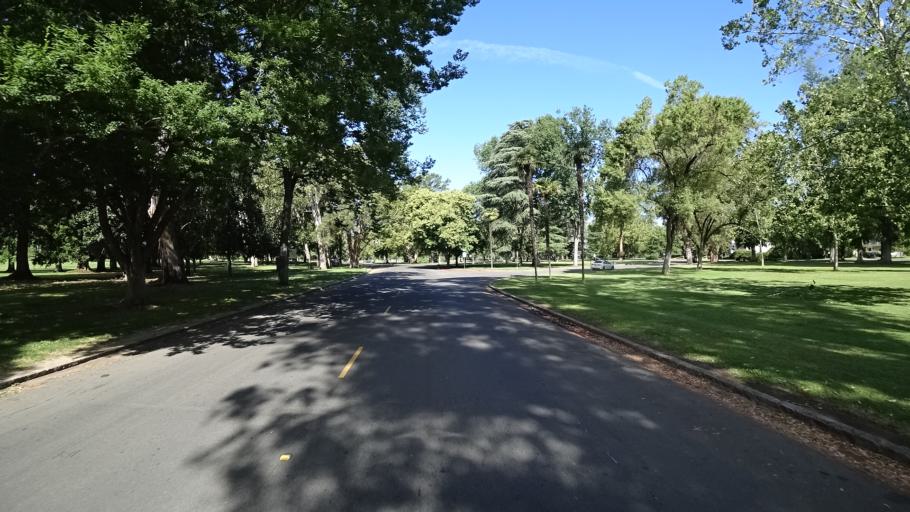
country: US
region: California
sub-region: Sacramento County
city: Sacramento
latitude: 38.5421
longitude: -121.4951
